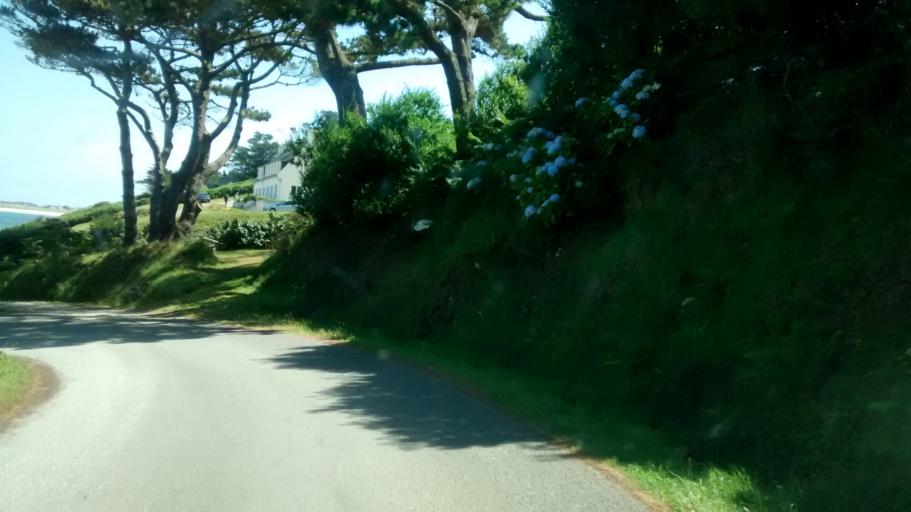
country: FR
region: Brittany
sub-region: Departement du Finistere
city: Plouguerneau
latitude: 48.6233
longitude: -4.4773
